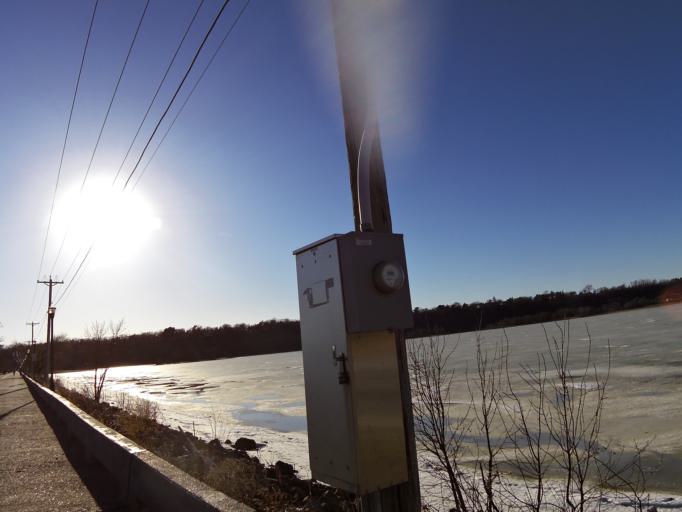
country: US
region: Wisconsin
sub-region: Saint Croix County
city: Hudson
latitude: 44.9745
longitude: -92.7602
